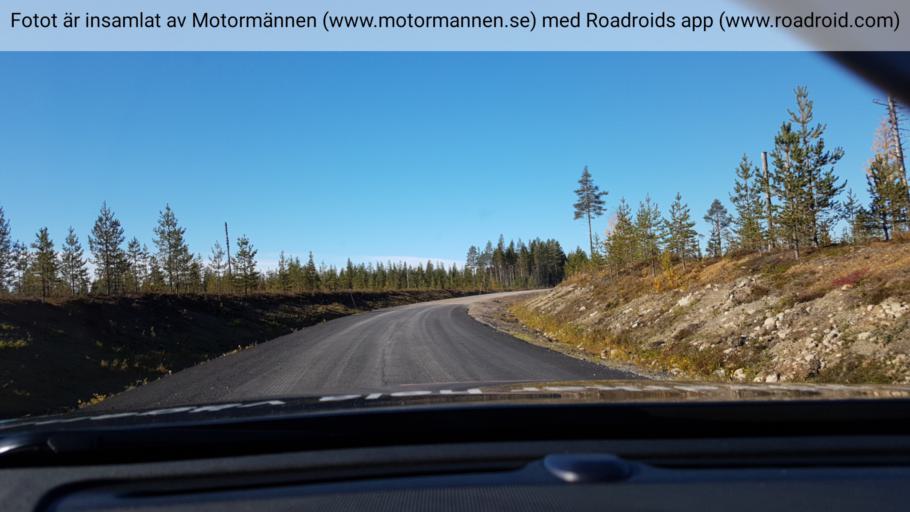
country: SE
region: Norrbotten
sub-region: Gallivare Kommun
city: Gaellivare
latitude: 66.5713
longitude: 21.0879
